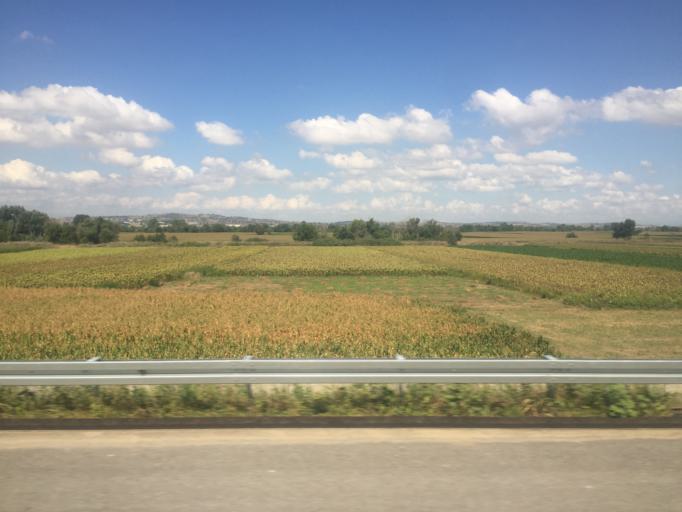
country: TR
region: Balikesir
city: Gobel
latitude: 40.0177
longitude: 28.2023
